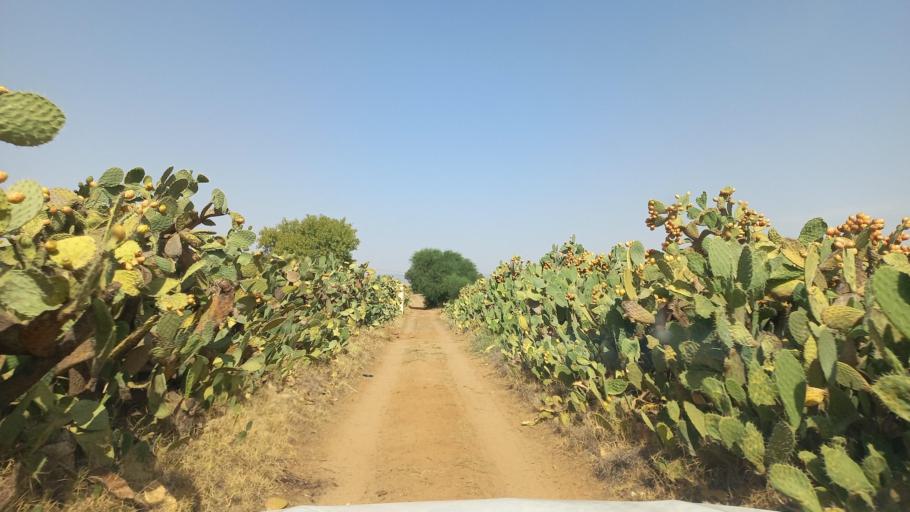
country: TN
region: Al Qasrayn
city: Kasserine
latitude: 35.2344
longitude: 9.0518
